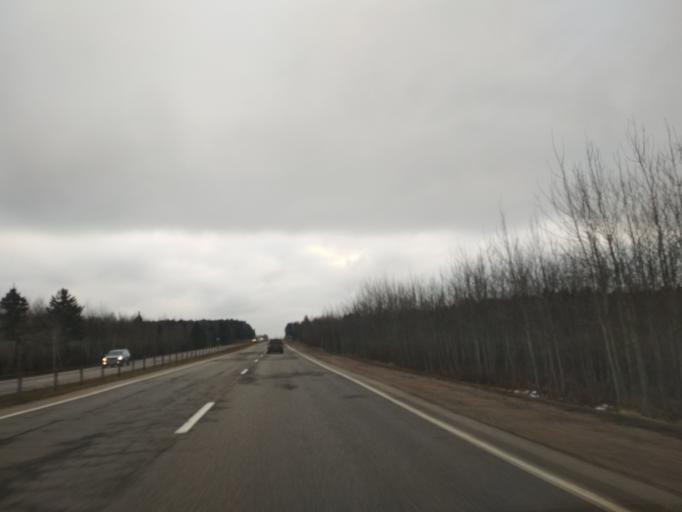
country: BY
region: Minsk
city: Luhavaya Slabada
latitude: 53.7201
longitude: 27.8632
